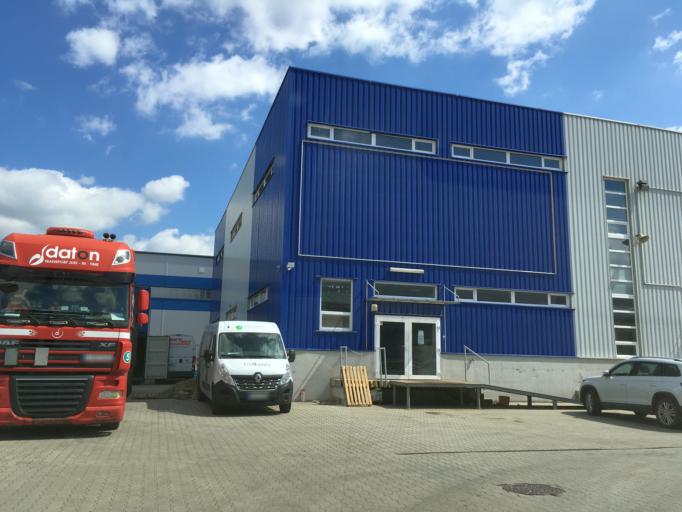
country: SK
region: Bratislavsky
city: Bratislava
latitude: 48.1882
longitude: 17.1652
